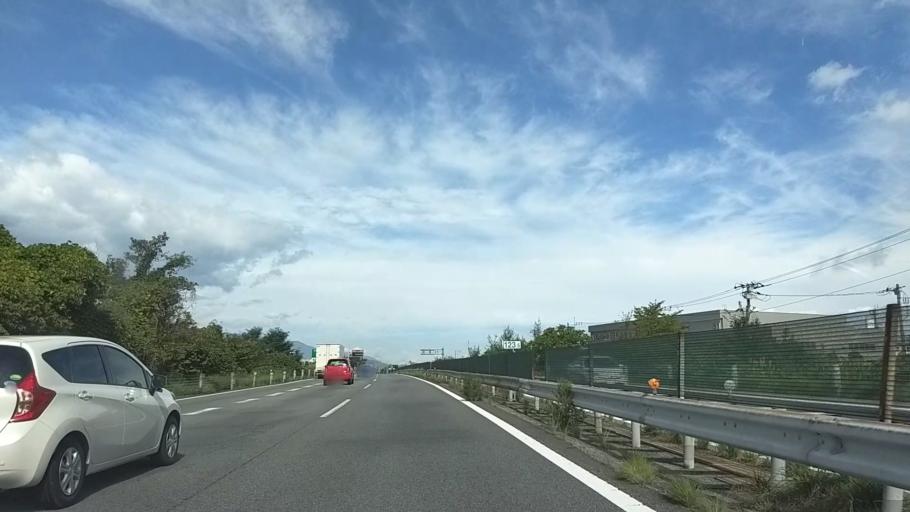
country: JP
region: Yamanashi
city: Nirasaki
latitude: 35.7139
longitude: 138.4708
